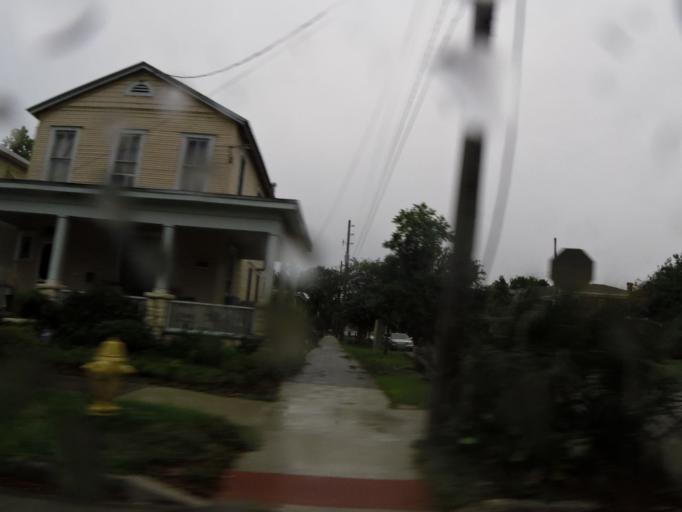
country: US
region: Florida
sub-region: Duval County
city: Jacksonville
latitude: 30.3373
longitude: -81.6488
